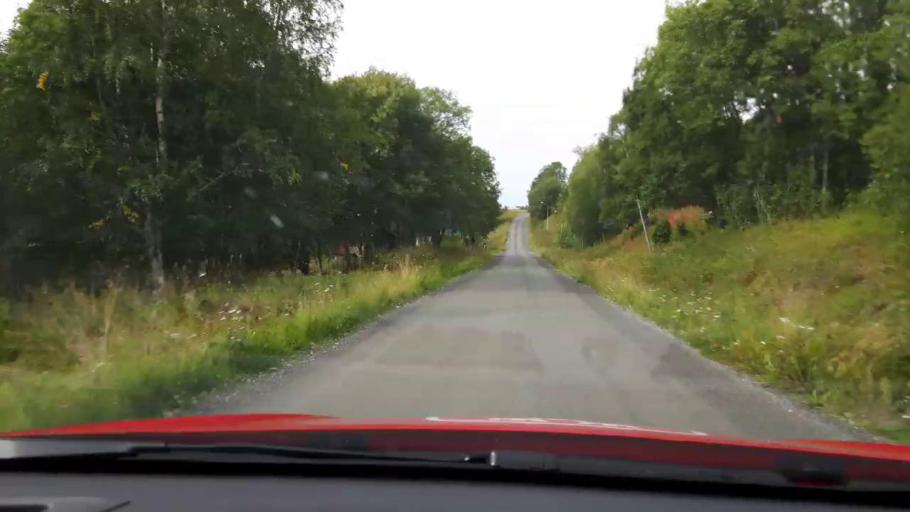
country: SE
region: Jaemtland
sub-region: Are Kommun
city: Are
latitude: 63.7489
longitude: 12.9633
